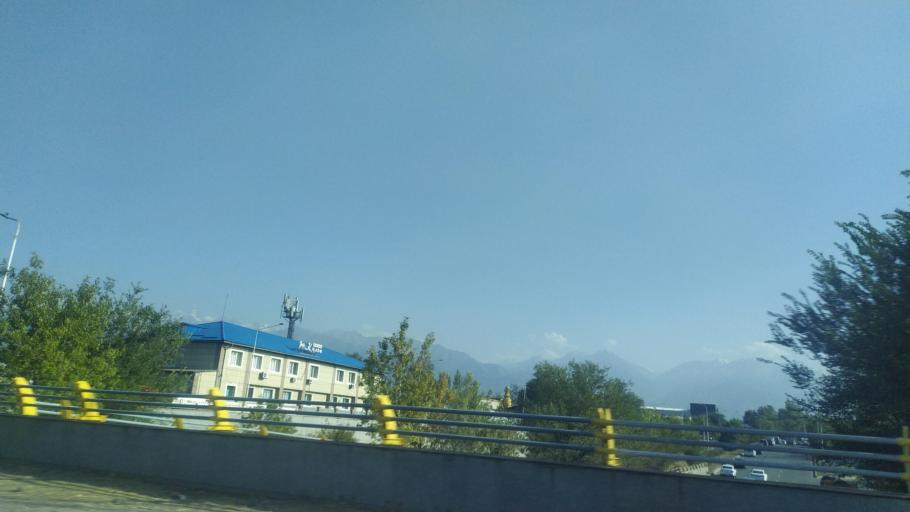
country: KZ
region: Almaty Qalasy
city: Almaty
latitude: 43.2721
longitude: 76.8862
